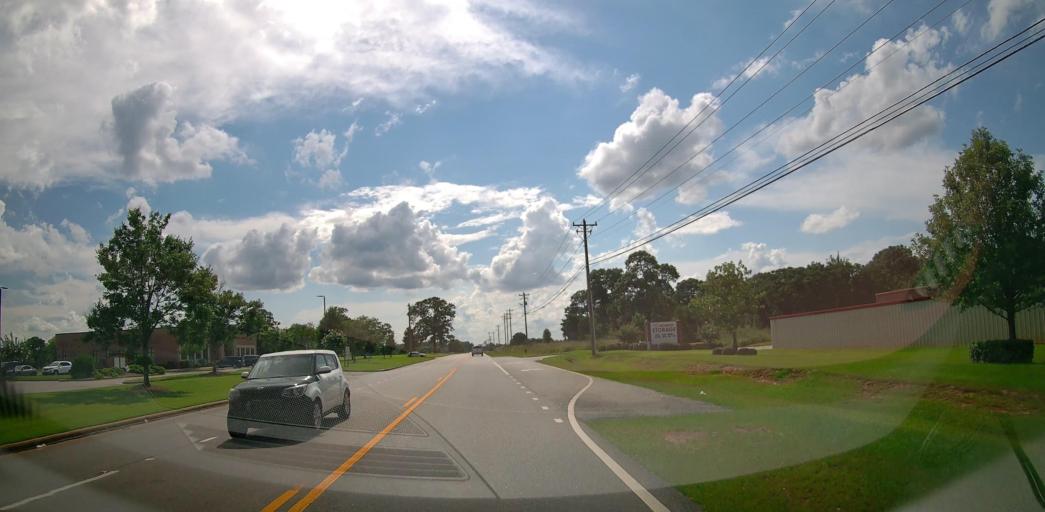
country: US
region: Georgia
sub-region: Houston County
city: Centerville
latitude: 32.5785
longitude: -83.7073
